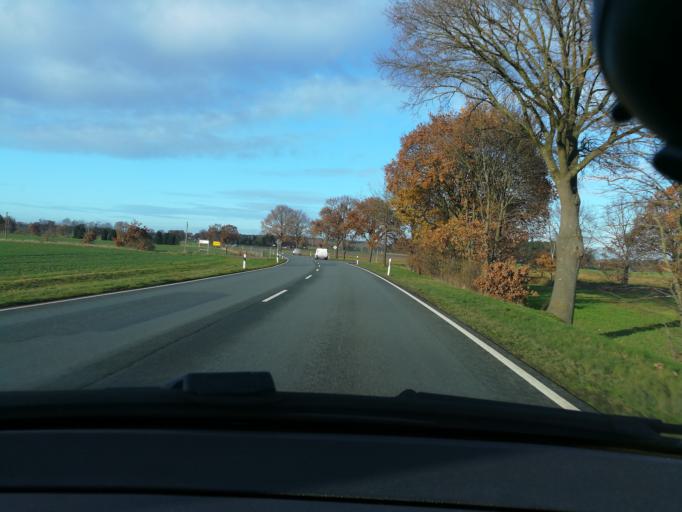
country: DE
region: Lower Saxony
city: Uchte
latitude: 52.5152
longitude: 8.9006
